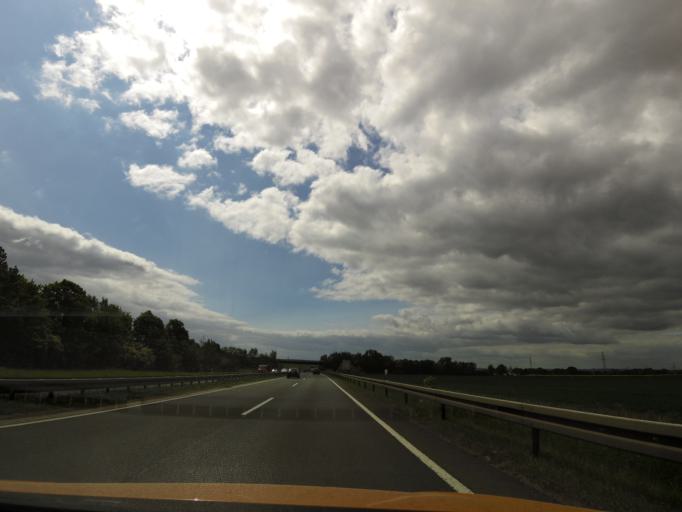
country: DE
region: Lower Saxony
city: Lengede
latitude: 52.1757
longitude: 10.3716
